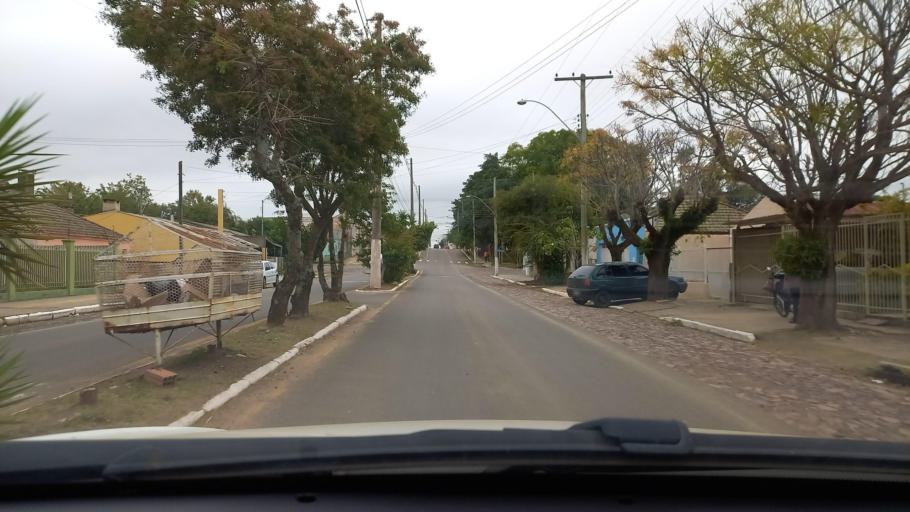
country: BR
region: Rio Grande do Sul
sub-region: Dom Pedrito
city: Dom Pedrito
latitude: -30.9845
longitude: -54.6671
